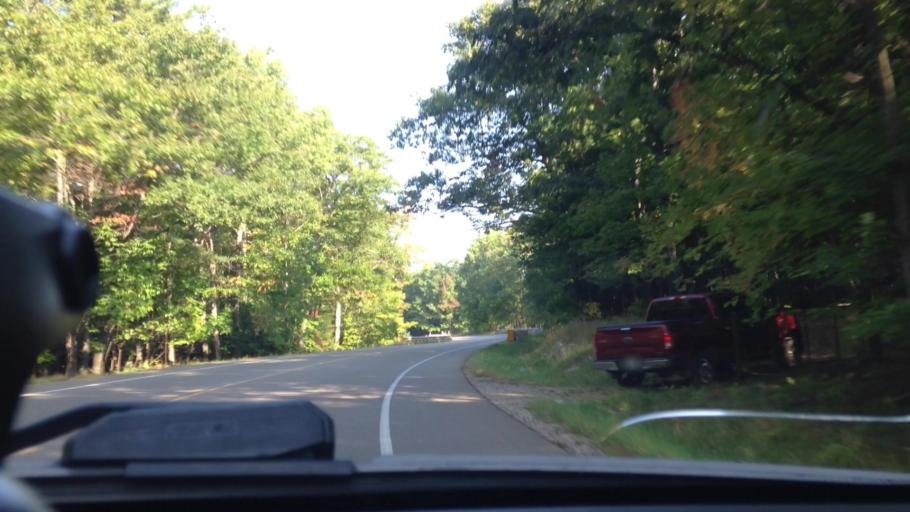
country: US
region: Michigan
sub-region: Dickinson County
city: Quinnesec
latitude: 45.8194
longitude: -87.9884
